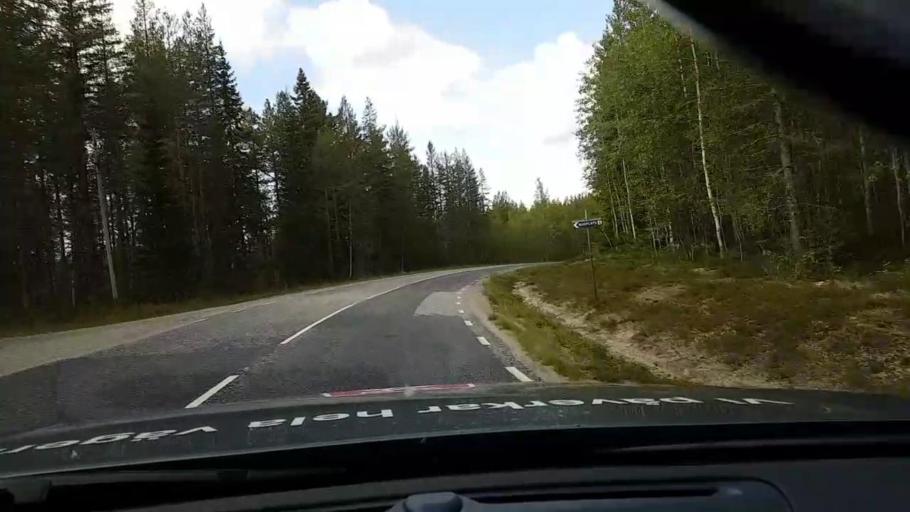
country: SE
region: Vaesterbotten
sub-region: Asele Kommun
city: Asele
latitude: 63.7930
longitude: 17.5779
